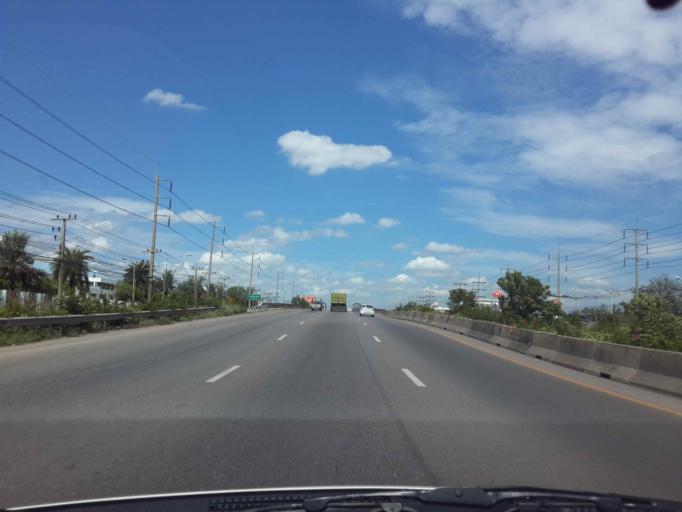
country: TH
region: Samut Sakhon
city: Ban Phaeo
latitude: 13.5209
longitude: 100.1735
